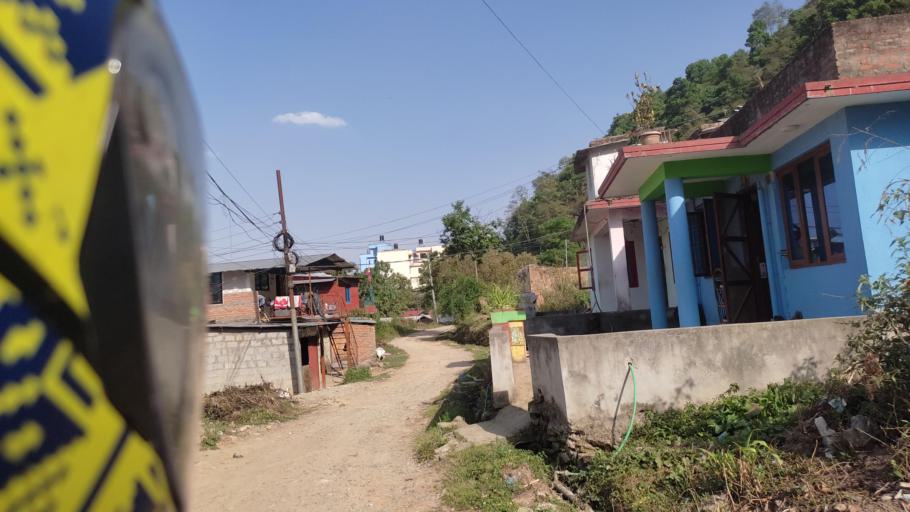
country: NP
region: Central Region
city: Kirtipur
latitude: 27.6570
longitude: 85.2658
